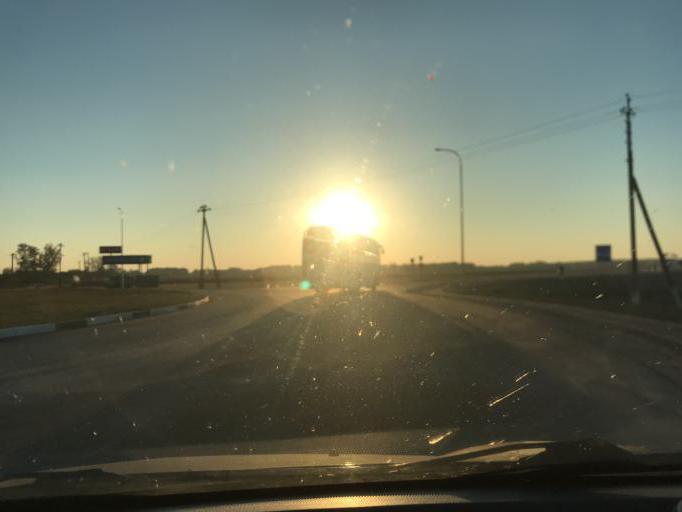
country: BY
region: Gomel
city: Brahin
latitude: 51.7768
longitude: 30.2495
